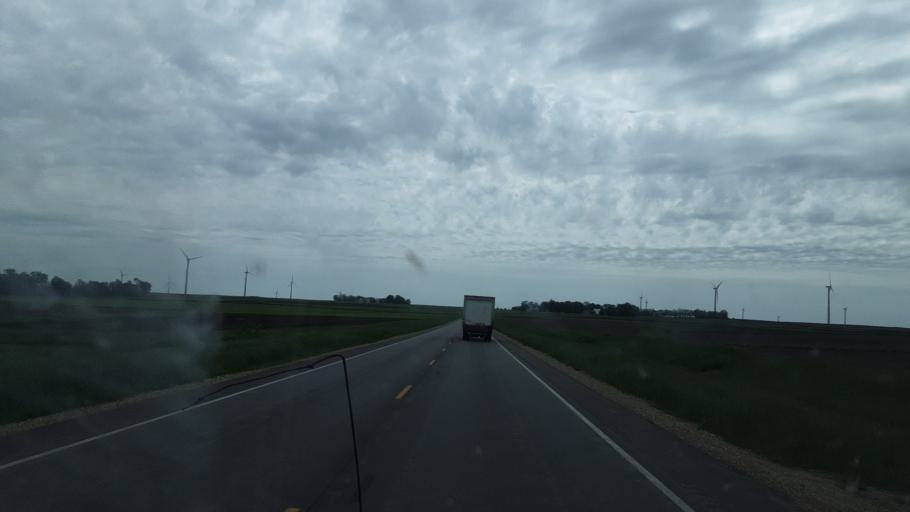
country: US
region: Illinois
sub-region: Tazewell County
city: Richmond
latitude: 40.3087
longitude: -89.4244
